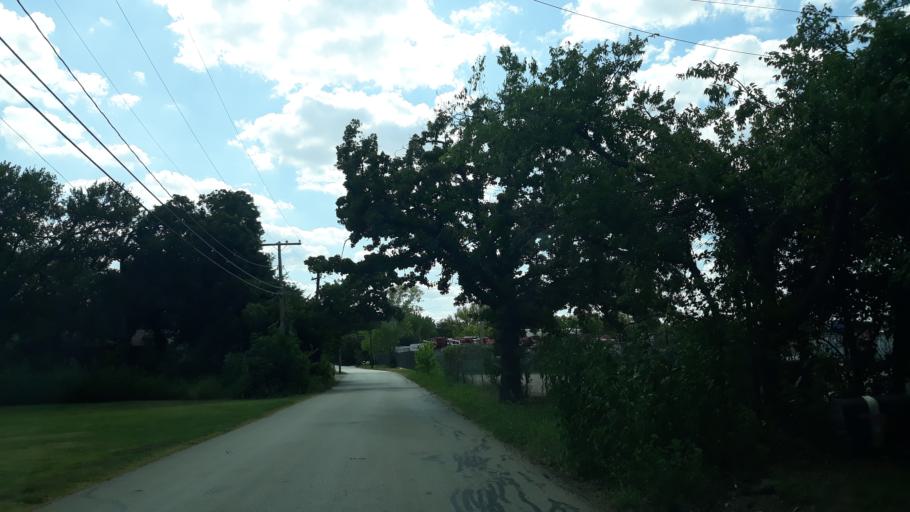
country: US
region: Texas
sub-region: Dallas County
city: Irving
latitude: 32.8144
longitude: -97.0031
